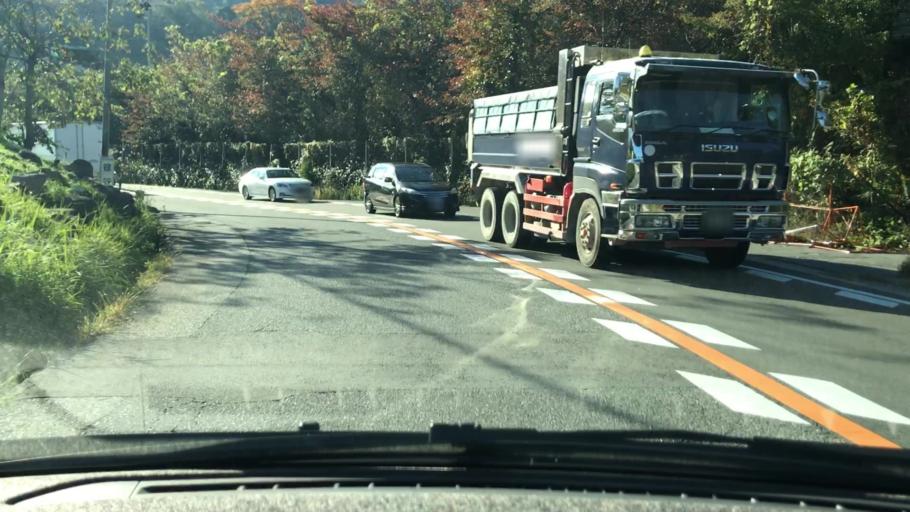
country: JP
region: Hyogo
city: Sandacho
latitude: 34.8320
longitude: 135.2849
